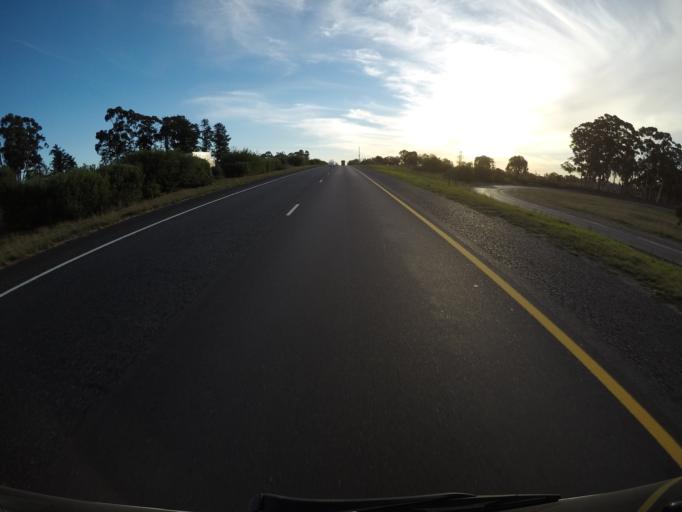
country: ZA
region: Western Cape
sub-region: City of Cape Town
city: Kraaifontein
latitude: -33.8199
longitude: 18.7909
